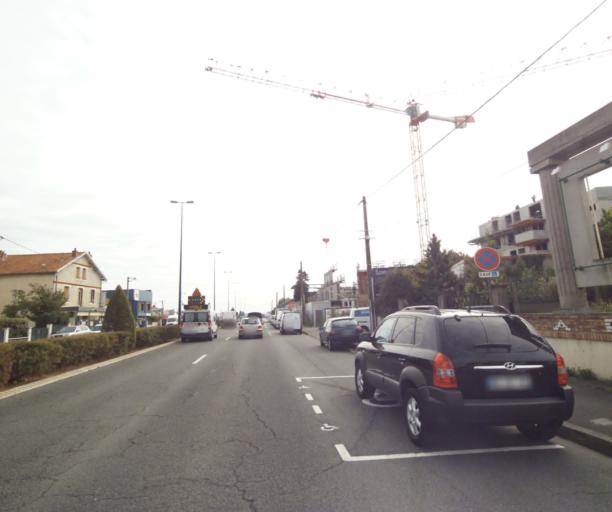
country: FR
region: Auvergne
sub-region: Departement du Puy-de-Dome
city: Aubiere
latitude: 45.7700
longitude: 3.1231
